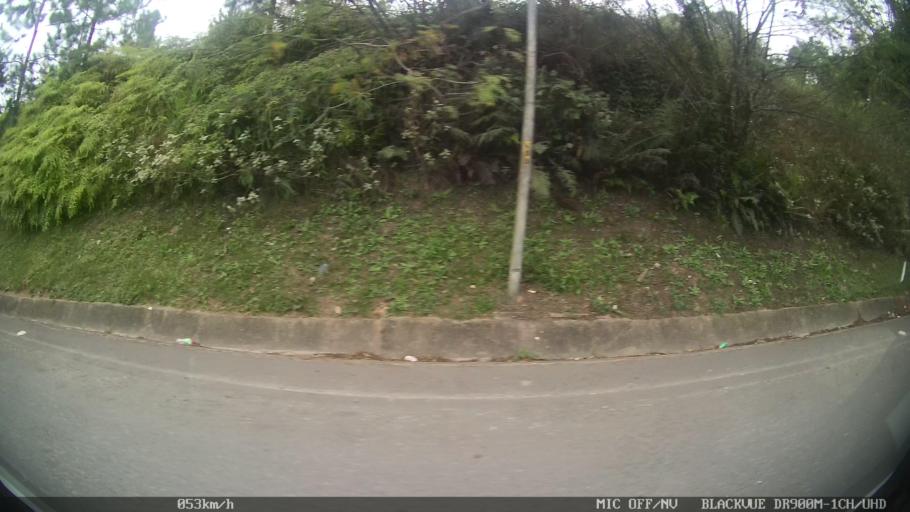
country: BR
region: Santa Catarina
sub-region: Joinville
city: Joinville
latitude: -26.3870
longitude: -48.8468
